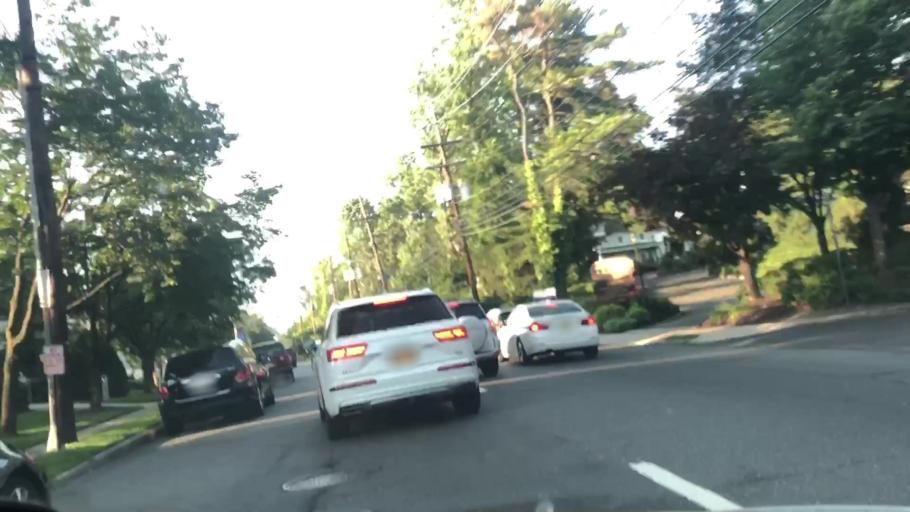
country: US
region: New Jersey
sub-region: Bergen County
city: Englewood
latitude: 40.8832
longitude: -73.9778
